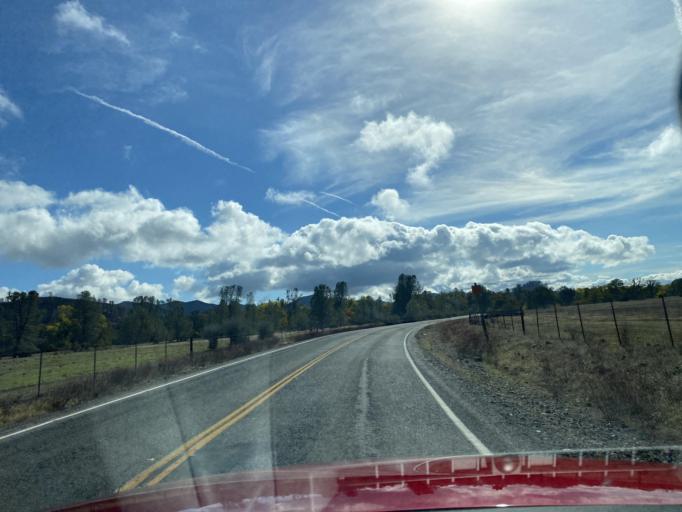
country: US
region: California
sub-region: Glenn County
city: Willows
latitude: 39.4390
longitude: -122.5064
